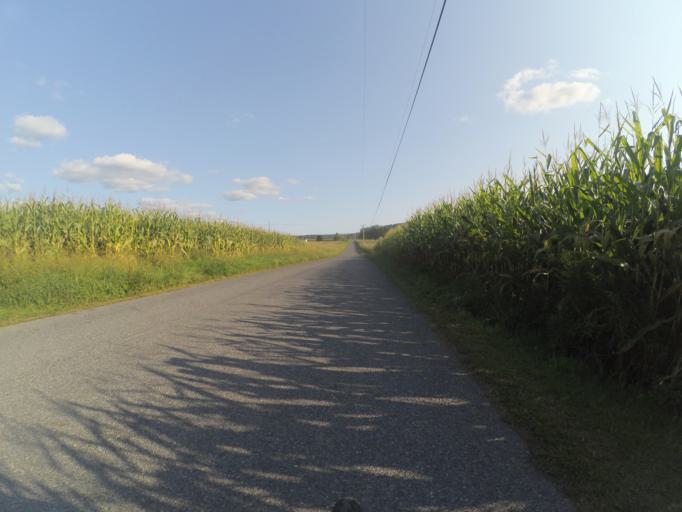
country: US
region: Pennsylvania
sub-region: Centre County
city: Centre Hall
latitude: 40.7995
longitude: -77.7052
